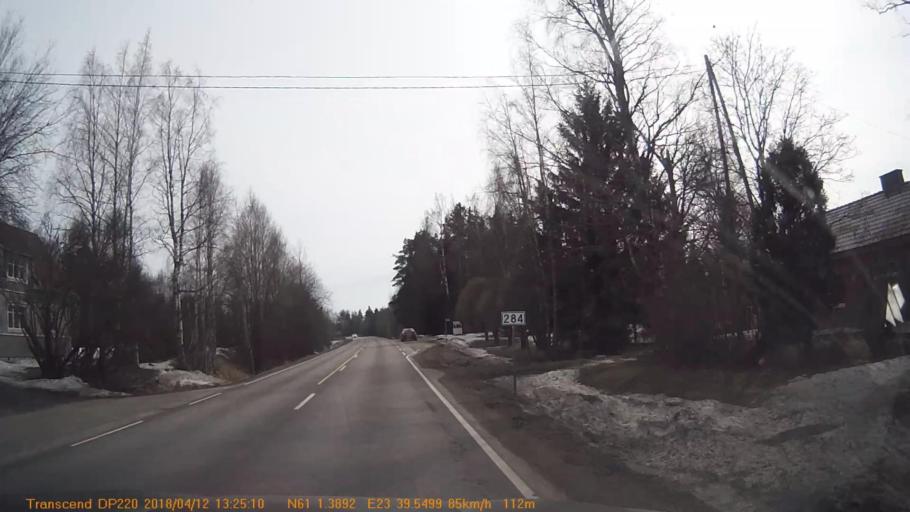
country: FI
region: Pirkanmaa
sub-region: Etelae-Pirkanmaa
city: Kylmaekoski
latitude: 61.0230
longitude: 23.6593
